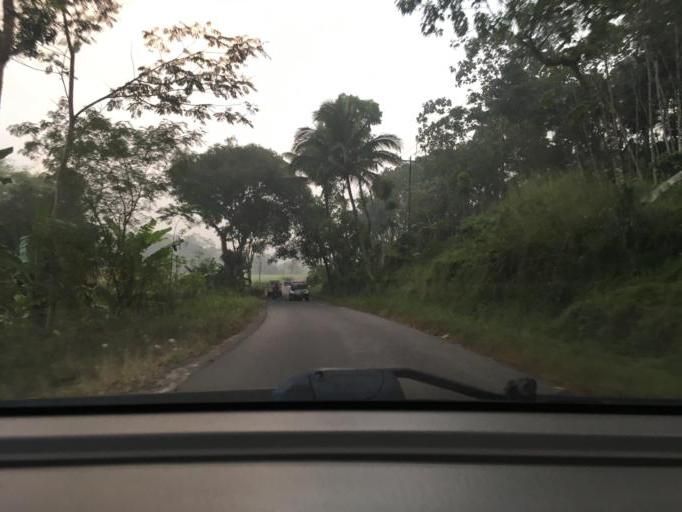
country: ID
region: West Java
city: Kampungdesa Pamokolan
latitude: -7.1912
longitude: 108.1981
